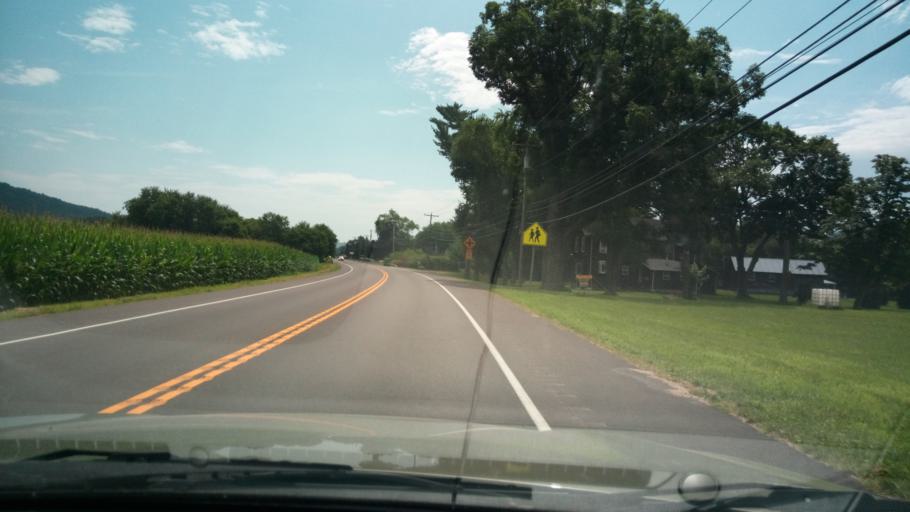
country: US
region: New York
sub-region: Chemung County
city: Southport
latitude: 42.0431
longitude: -76.7650
